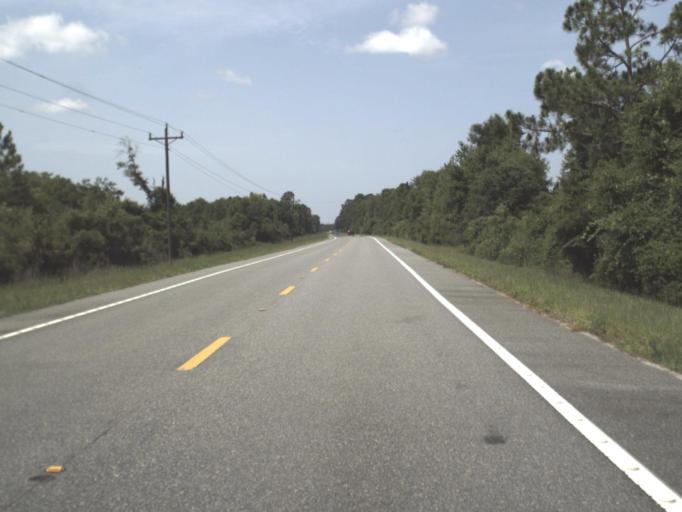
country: US
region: Florida
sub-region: Taylor County
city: Steinhatchee
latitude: 29.7442
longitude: -83.3552
